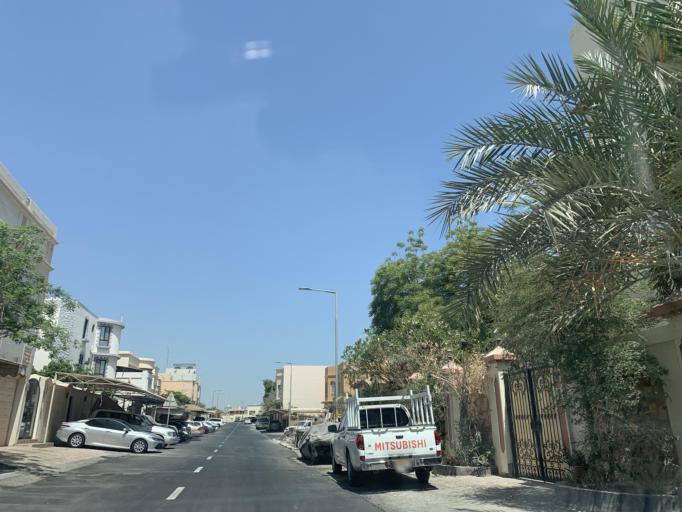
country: BH
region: Northern
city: Ar Rifa'
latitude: 26.1363
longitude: 50.5756
